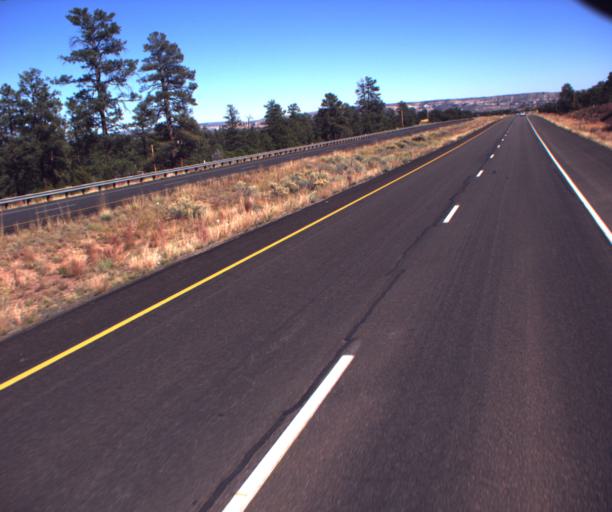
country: US
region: Arizona
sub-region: Apache County
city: Saint Michaels
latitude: 35.6584
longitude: -109.1315
